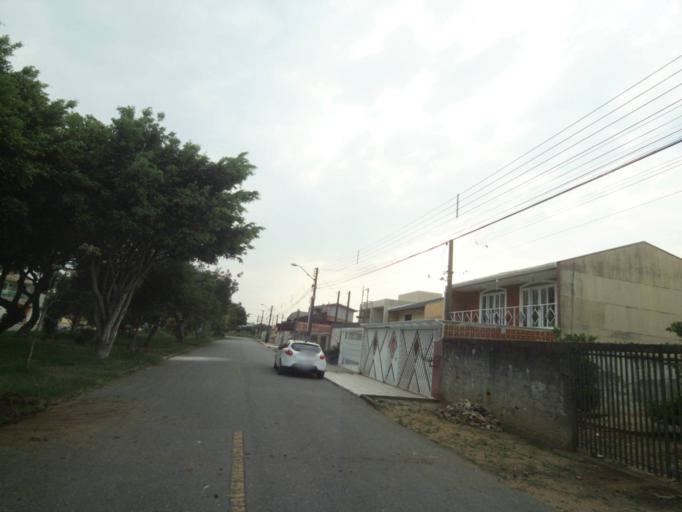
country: BR
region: Parana
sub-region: Sao Jose Dos Pinhais
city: Sao Jose dos Pinhais
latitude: -25.5341
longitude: -49.2512
